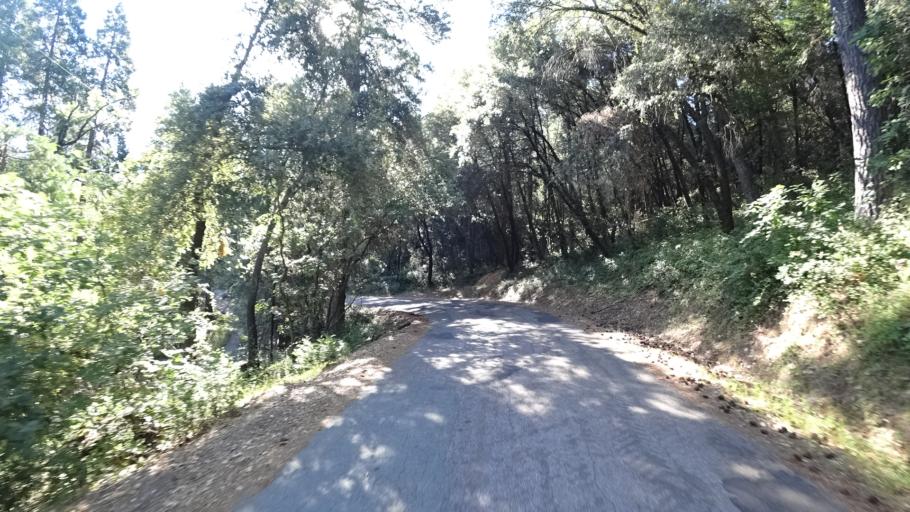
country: US
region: California
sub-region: Amador County
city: Pioneer
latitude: 38.4101
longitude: -120.5583
